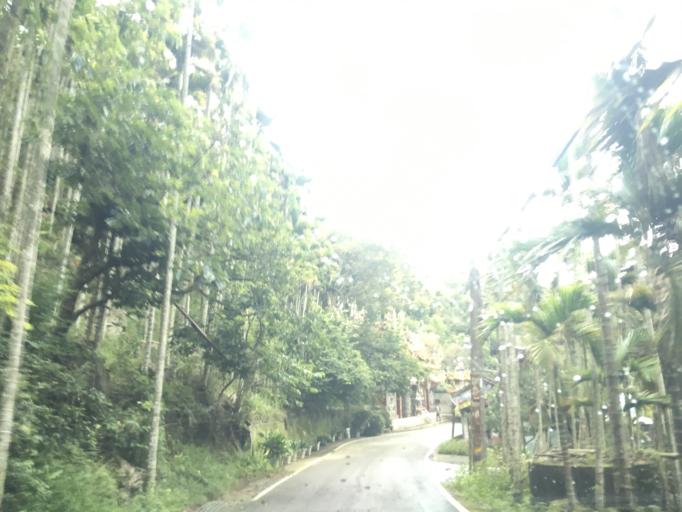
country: TW
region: Taiwan
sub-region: Yunlin
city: Douliu
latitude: 23.5640
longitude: 120.6241
